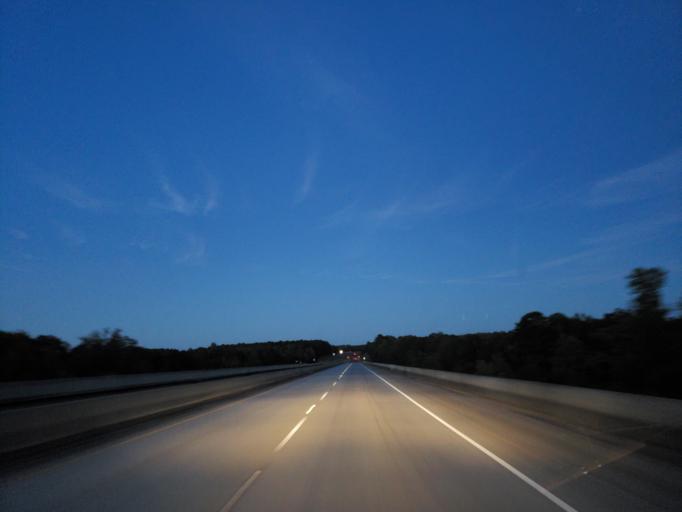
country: US
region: Mississippi
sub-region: Clarke County
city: Quitman
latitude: 31.9825
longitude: -88.7160
